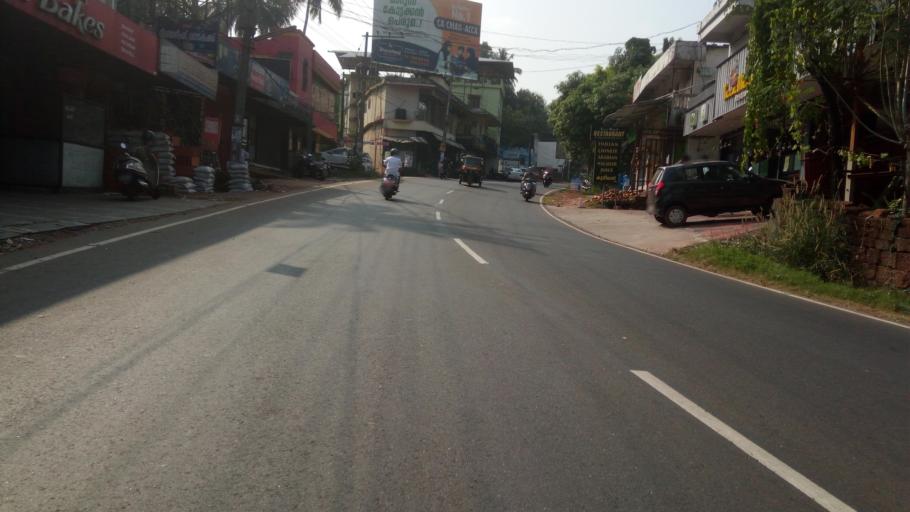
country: IN
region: Kerala
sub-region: Malappuram
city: Malappuram
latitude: 11.0034
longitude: 76.0116
